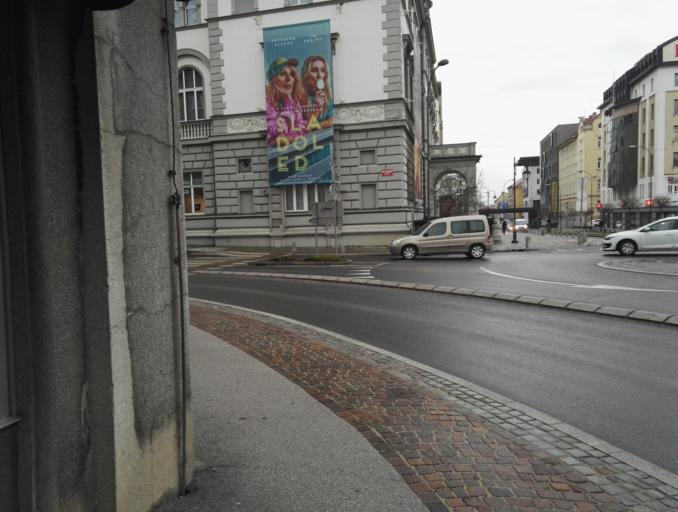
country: SI
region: Maribor
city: Maribor
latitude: 46.5576
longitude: 15.6486
